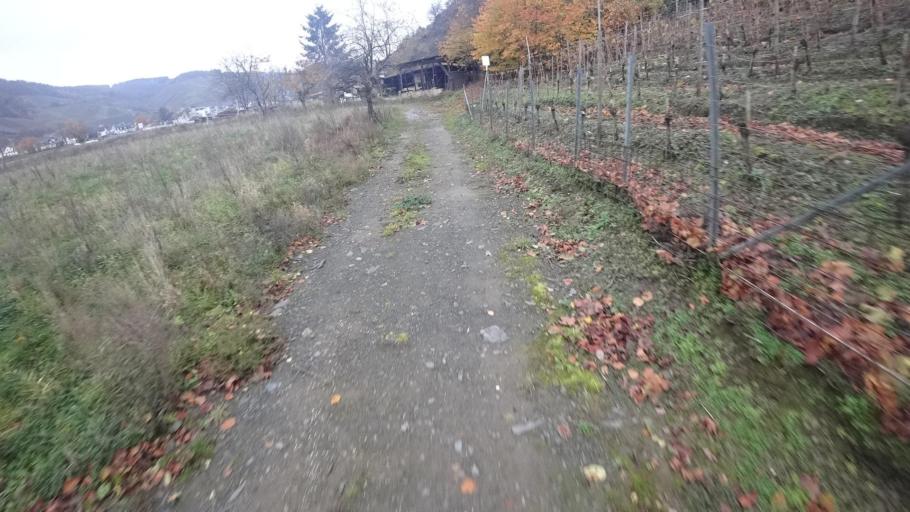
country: DE
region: Rheinland-Pfalz
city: Dernau
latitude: 50.5254
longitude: 7.0423
